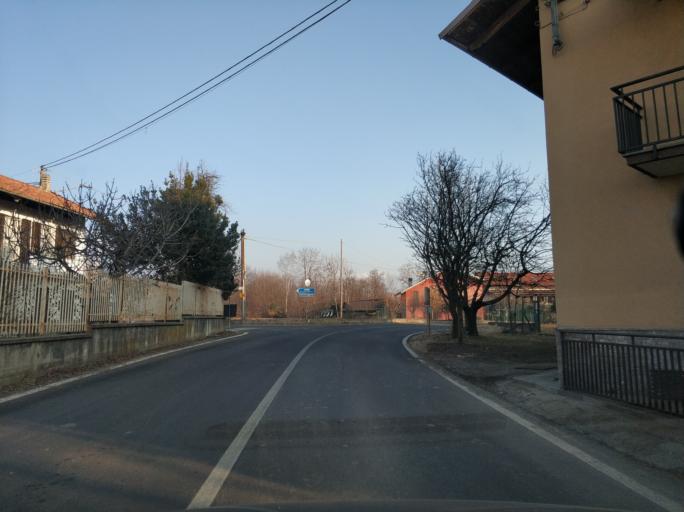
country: IT
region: Piedmont
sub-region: Provincia di Torino
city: Rocca Canavese
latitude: 45.2808
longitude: 7.5816
